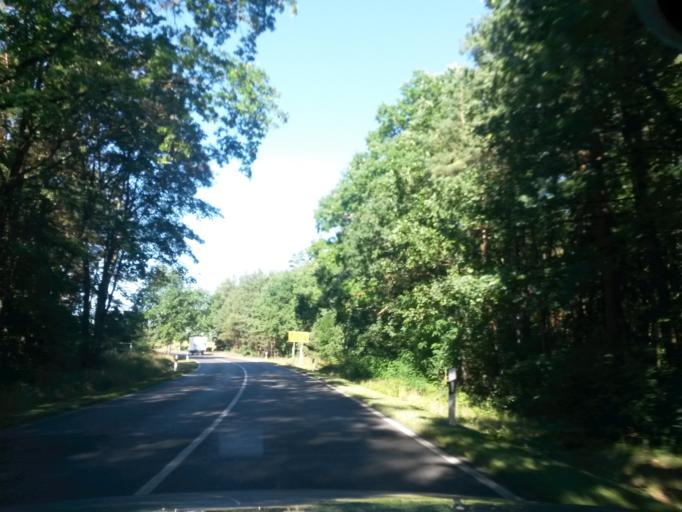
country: DE
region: Brandenburg
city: Lychen
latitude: 53.1466
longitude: 13.3919
